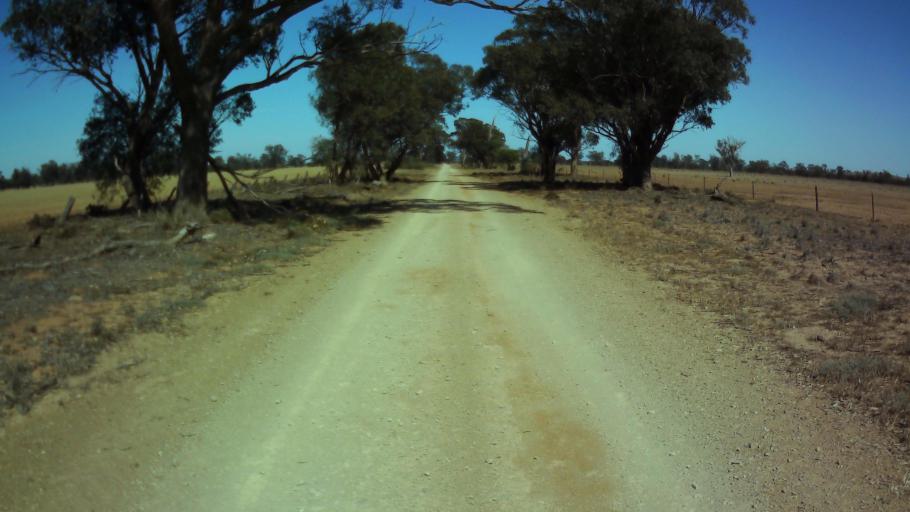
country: AU
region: New South Wales
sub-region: Weddin
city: Grenfell
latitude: -33.8731
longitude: 147.8695
